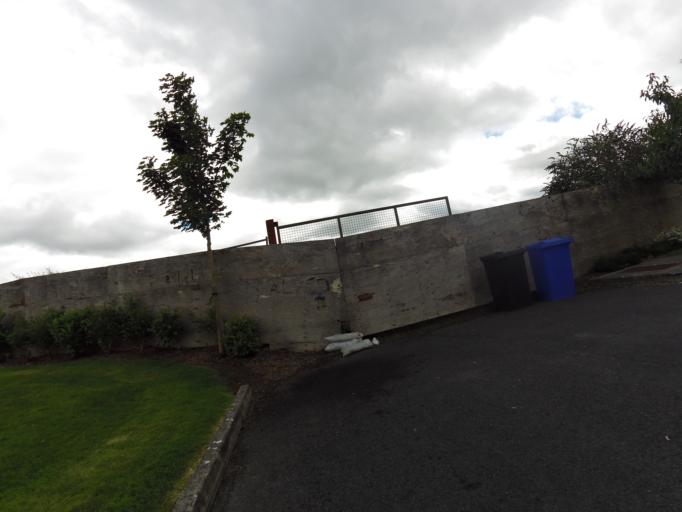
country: IE
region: Connaught
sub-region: County Galway
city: Athenry
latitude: 53.3027
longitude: -8.7400
